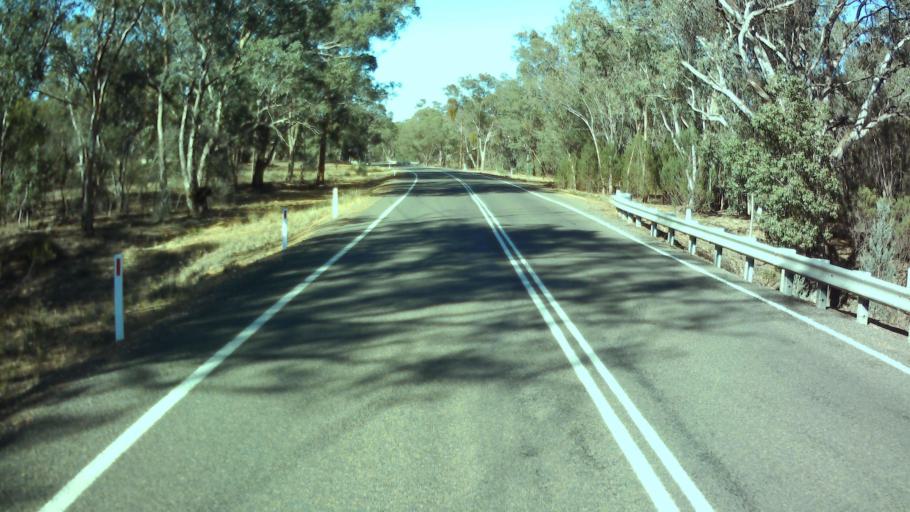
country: AU
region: New South Wales
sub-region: Weddin
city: Grenfell
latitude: -34.0021
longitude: 148.1276
